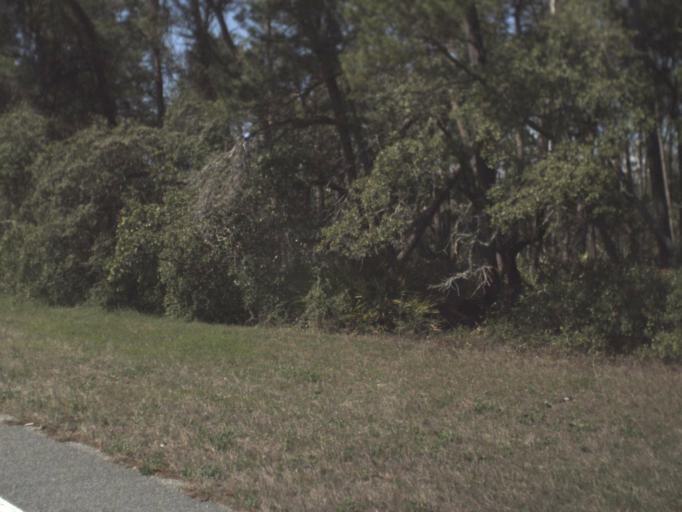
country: US
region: Florida
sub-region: Wakulla County
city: Crawfordville
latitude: 29.9253
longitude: -84.4200
